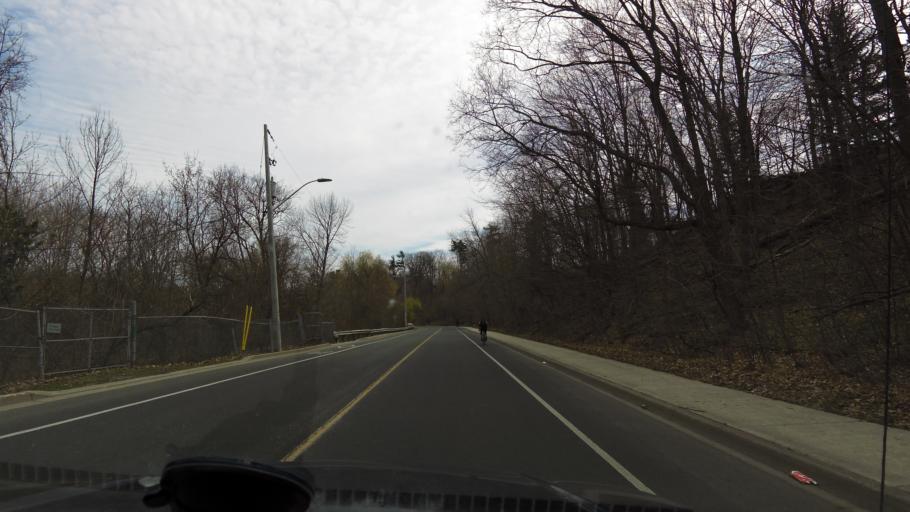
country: CA
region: Ontario
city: Mississauga
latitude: 43.5410
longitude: -79.6550
